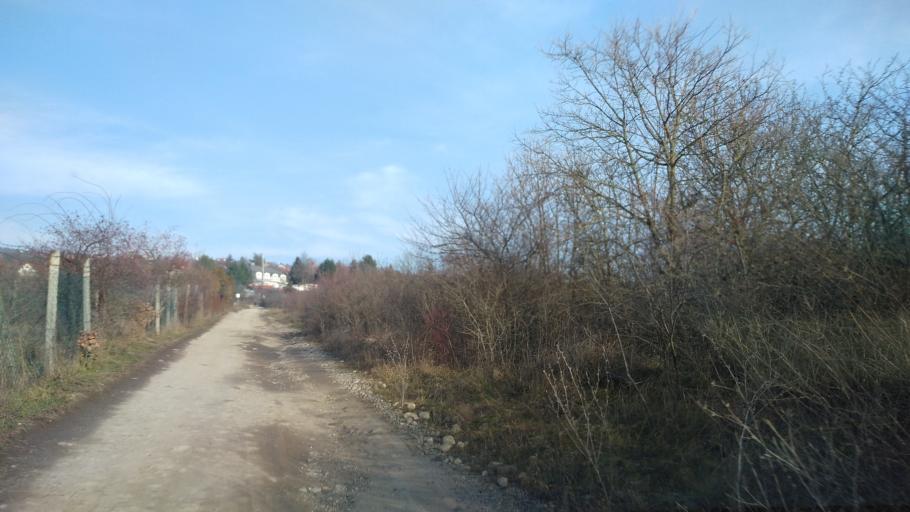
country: HU
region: Pest
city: Szentendre
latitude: 47.6894
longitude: 19.0576
